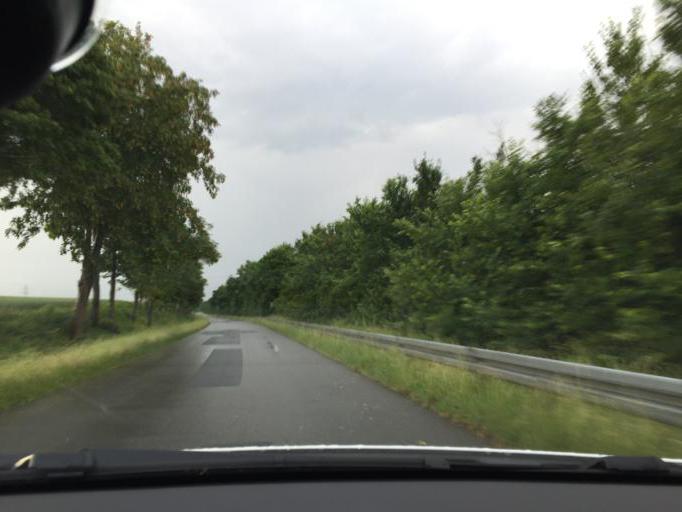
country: DE
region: Lower Saxony
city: Hehlen
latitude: 52.0277
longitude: 9.4122
